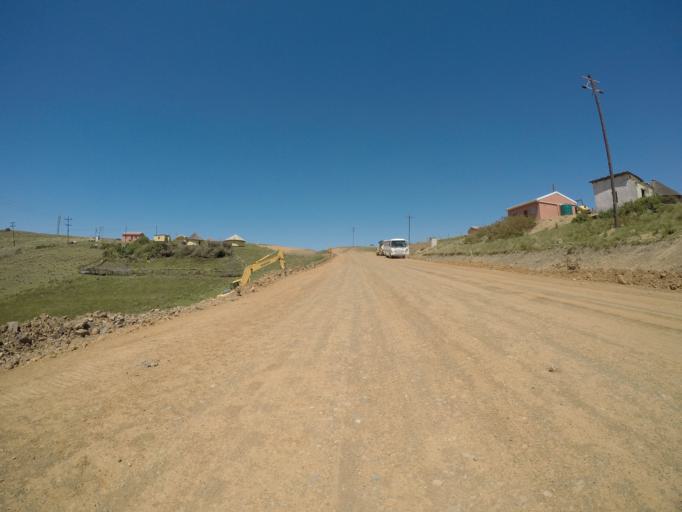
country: ZA
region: Eastern Cape
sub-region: OR Tambo District Municipality
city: Libode
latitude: -32.0219
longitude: 29.1147
